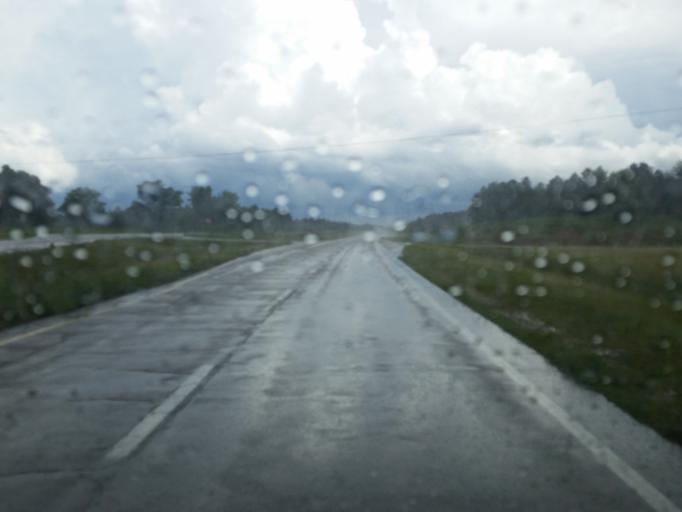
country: US
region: Mississippi
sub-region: George County
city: Lucedale
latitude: 30.8948
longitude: -88.4522
